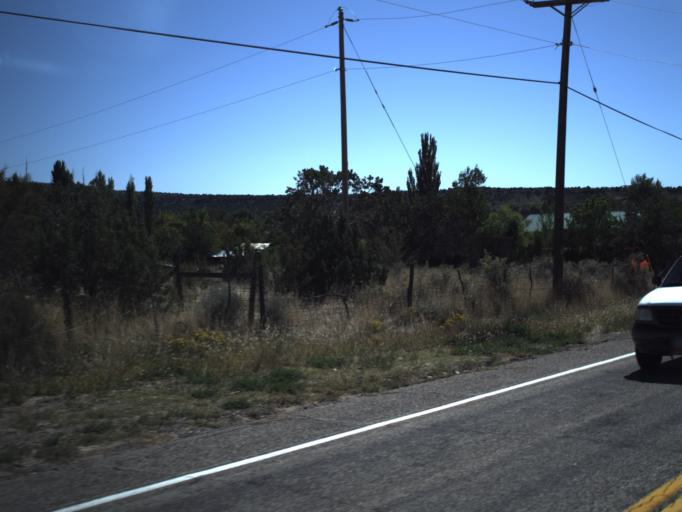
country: US
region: Utah
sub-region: Washington County
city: Ivins
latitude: 37.3409
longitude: -113.6933
